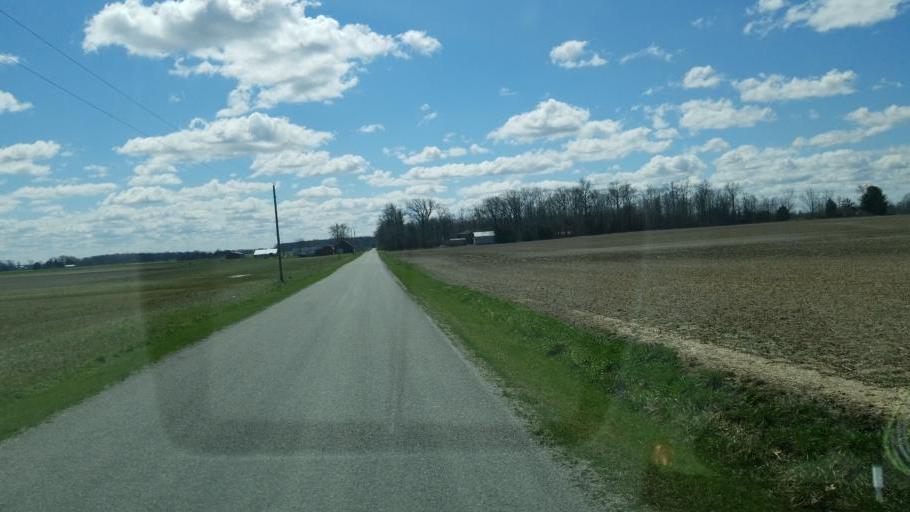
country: US
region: Ohio
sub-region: Hancock County
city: Findlay
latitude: 41.0494
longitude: -83.5151
